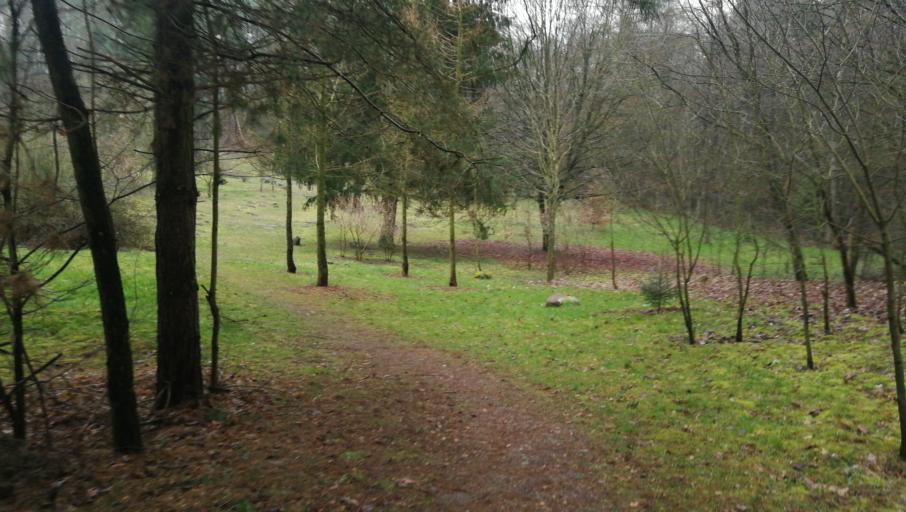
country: PL
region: Kujawsko-Pomorskie
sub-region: Powiat brodnicki
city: Gorzno
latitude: 53.1934
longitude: 19.6568
